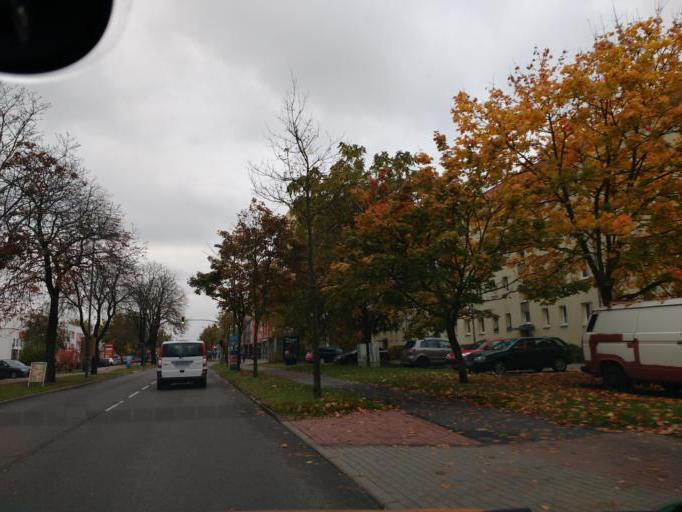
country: DE
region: Brandenburg
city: Ludwigsfelde
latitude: 52.3063
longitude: 13.2507
